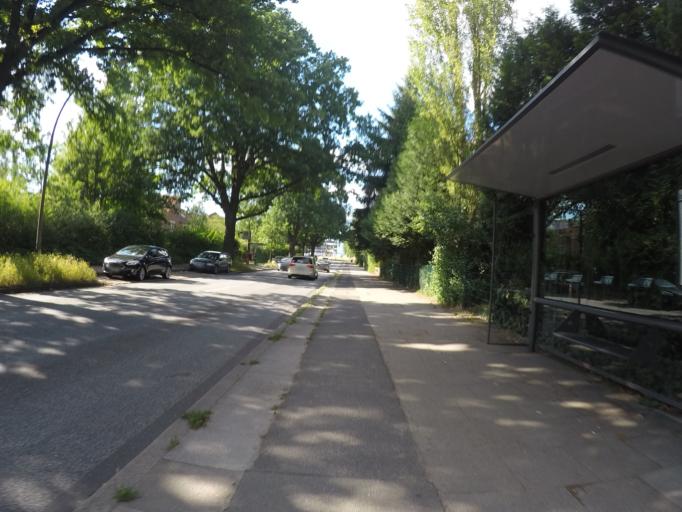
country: DE
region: Hamburg
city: Alsterdorf
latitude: 53.6155
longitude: 10.0078
